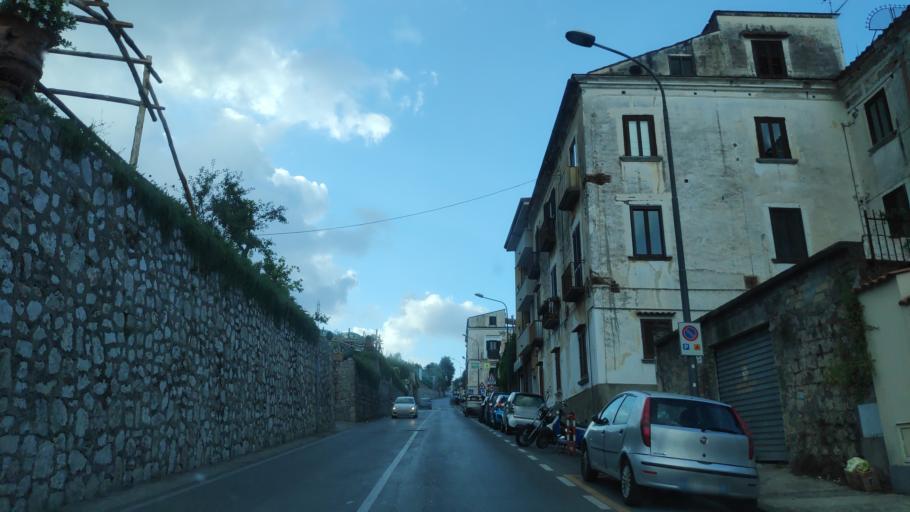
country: IT
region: Campania
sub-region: Provincia di Napoli
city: Piano di Sorrento
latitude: 40.6321
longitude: 14.4191
